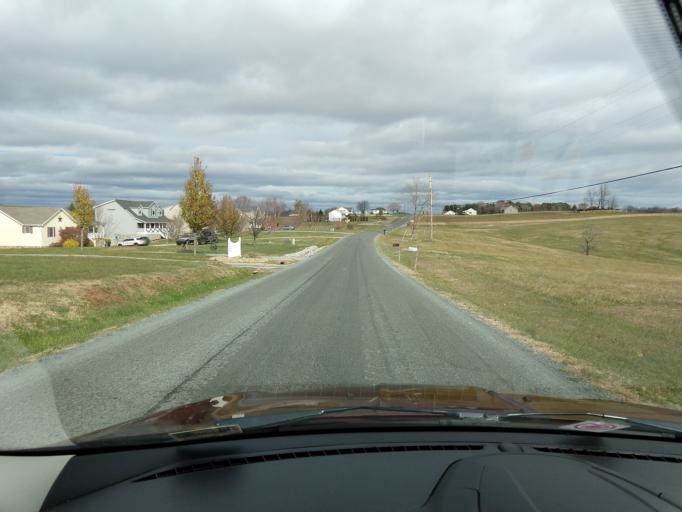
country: US
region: Virginia
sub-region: Franklin County
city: North Shore
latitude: 37.2079
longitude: -79.6843
